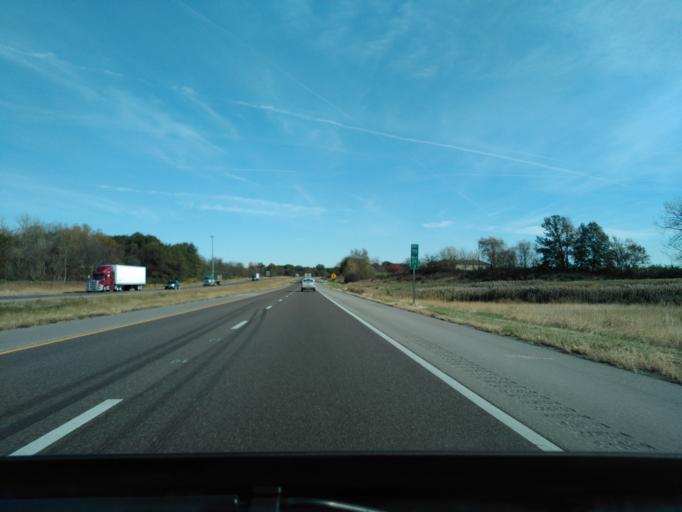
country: US
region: Illinois
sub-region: Madison County
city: Saint Jacob
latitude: 38.7770
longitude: -89.7421
